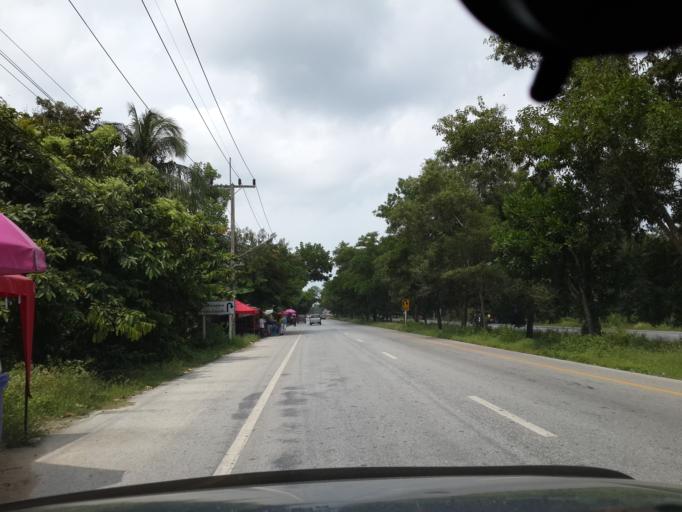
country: TH
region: Pattani
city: Yaring
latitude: 6.8646
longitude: 101.3629
